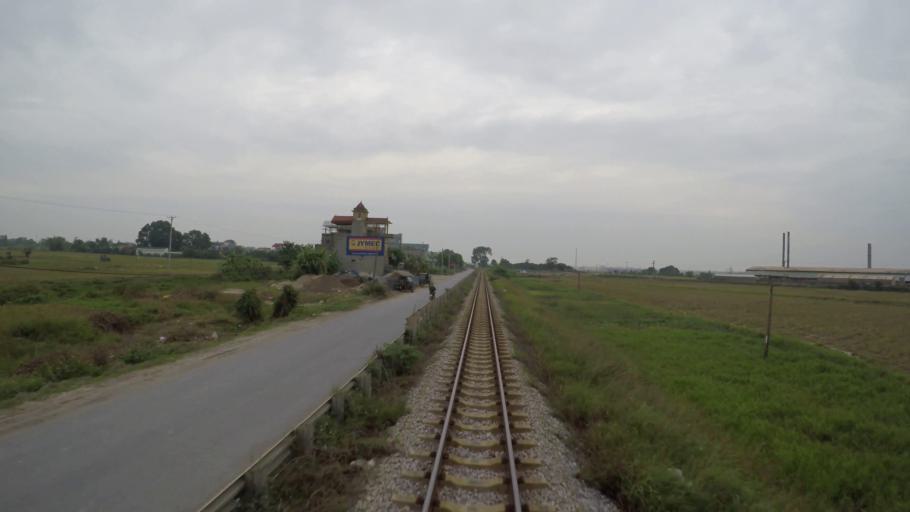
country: VN
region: Hung Yen
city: Ban Yen Nhan
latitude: 20.9702
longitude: 106.1014
